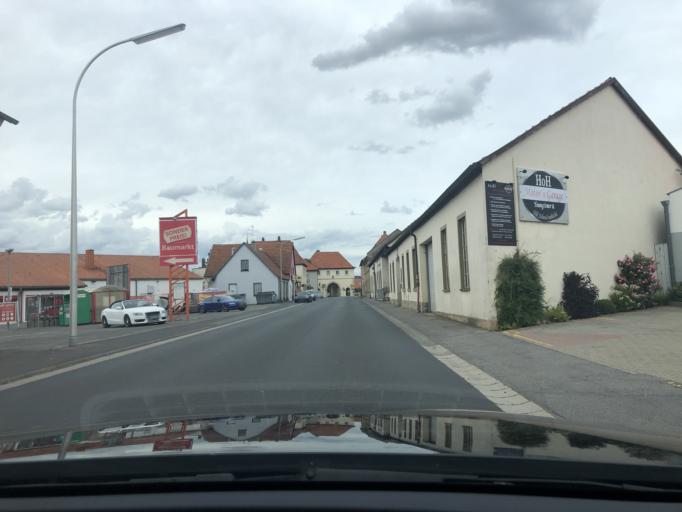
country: DE
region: Bavaria
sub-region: Regierungsbezirk Unterfranken
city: Hofheim in Unterfranken
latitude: 50.1335
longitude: 10.5224
